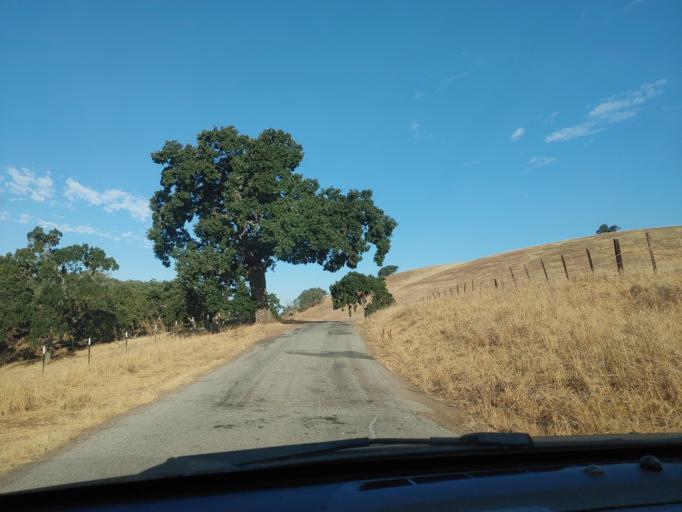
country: US
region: California
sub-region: San Benito County
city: Ridgemark
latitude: 36.7697
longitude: -121.2092
